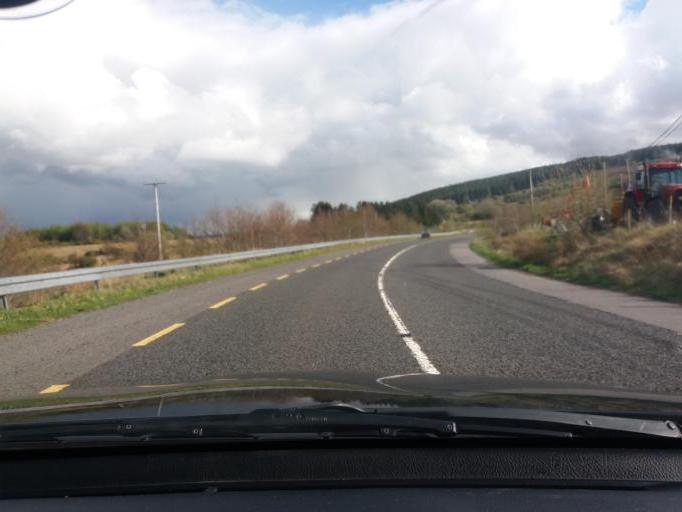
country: IE
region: Connaught
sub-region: County Leitrim
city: Manorhamilton
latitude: 54.3473
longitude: -8.2373
